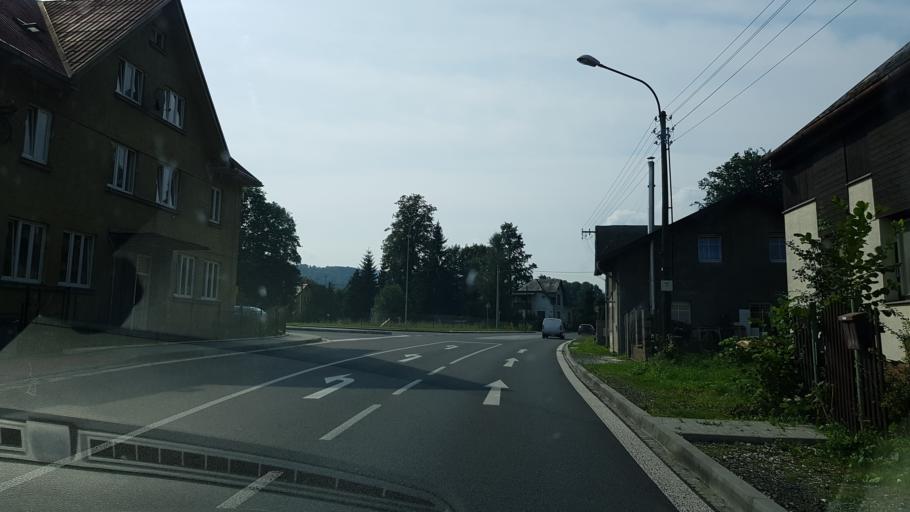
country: CZ
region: Olomoucky
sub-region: Okres Jesenik
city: Jesenik
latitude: 50.2202
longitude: 17.2081
